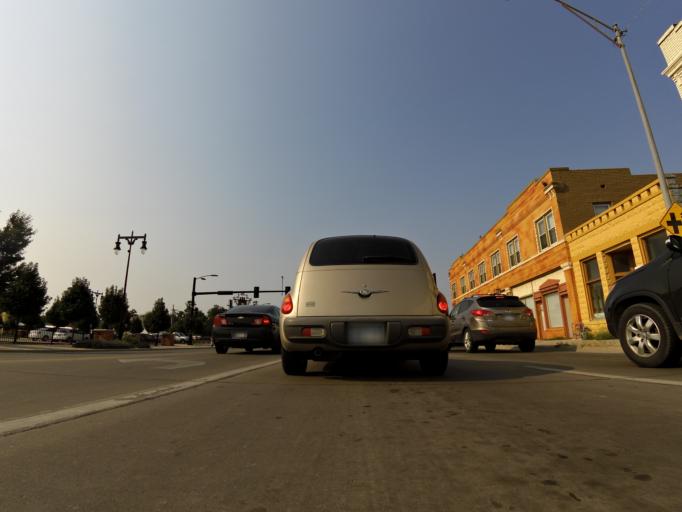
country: US
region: Kansas
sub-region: Sedgwick County
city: Wichita
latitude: 37.7222
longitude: -97.3356
